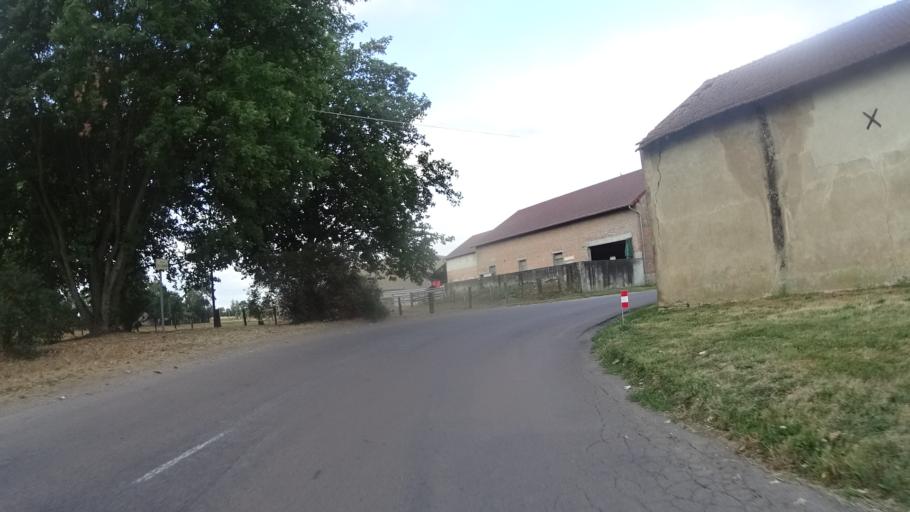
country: FR
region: Bourgogne
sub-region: Departement de la Cote-d'Or
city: Seurre
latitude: 46.9752
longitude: 5.1000
